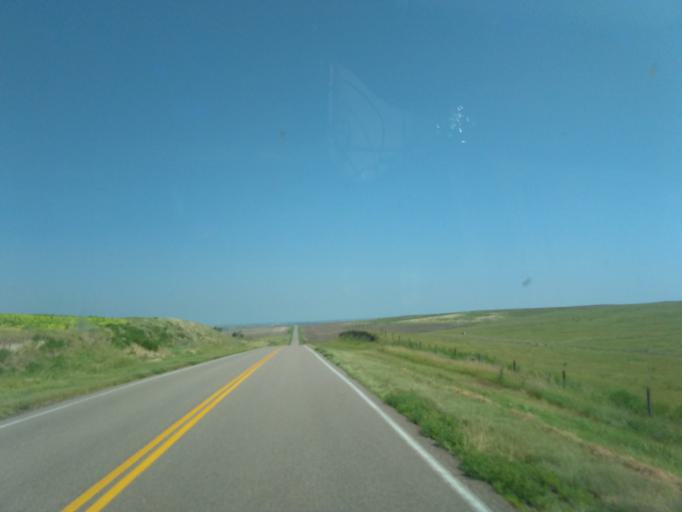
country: US
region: Nebraska
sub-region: Dundy County
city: Benkelman
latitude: 39.9570
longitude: -101.5415
